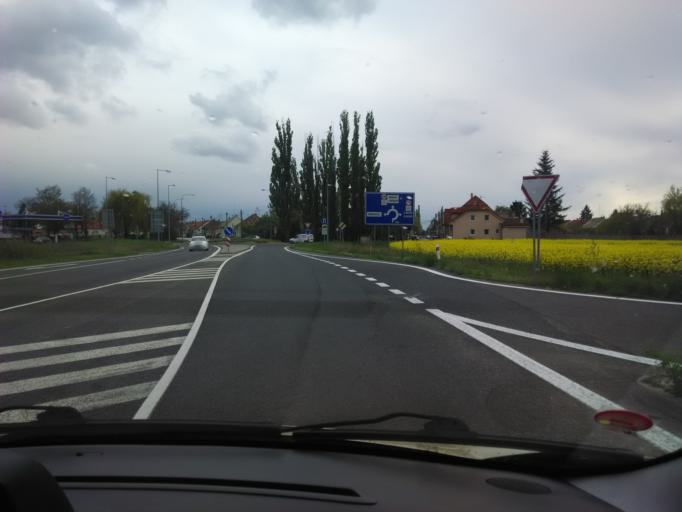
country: SK
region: Trnavsky
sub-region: Okres Trnava
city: Trnava
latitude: 48.3970
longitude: 17.5987
